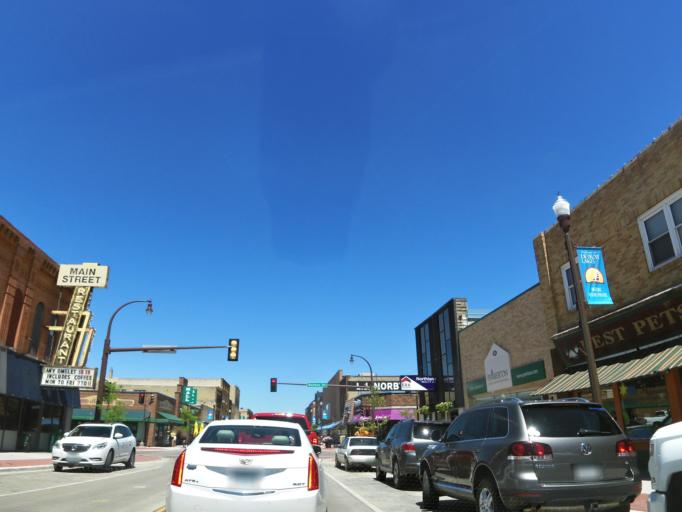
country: US
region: Minnesota
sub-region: Becker County
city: Detroit Lakes
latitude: 46.8169
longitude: -95.8453
